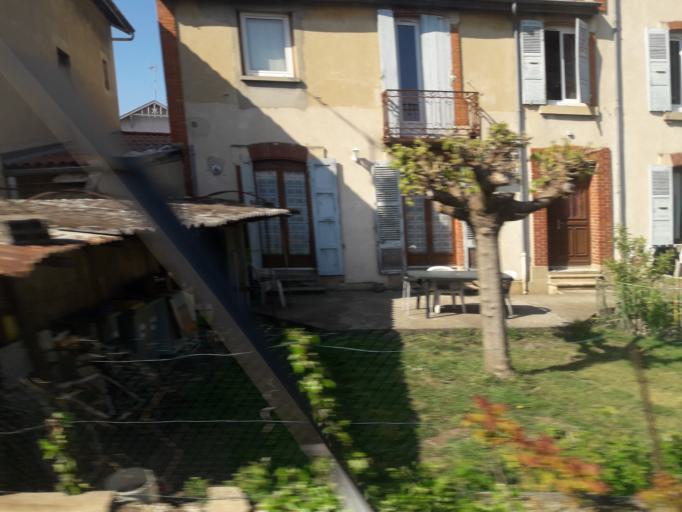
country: FR
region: Rhone-Alpes
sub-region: Departement de la Drome
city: Romans-sur-Isere
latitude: 45.0483
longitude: 5.0598
